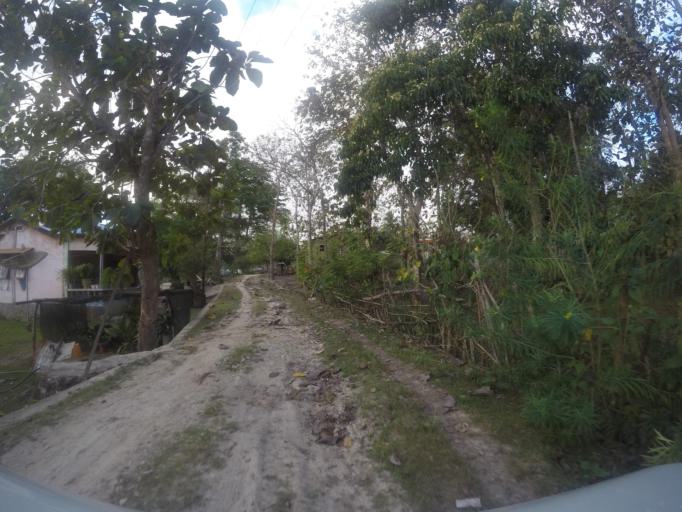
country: TL
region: Lautem
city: Lospalos
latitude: -8.5161
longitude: 126.9871
